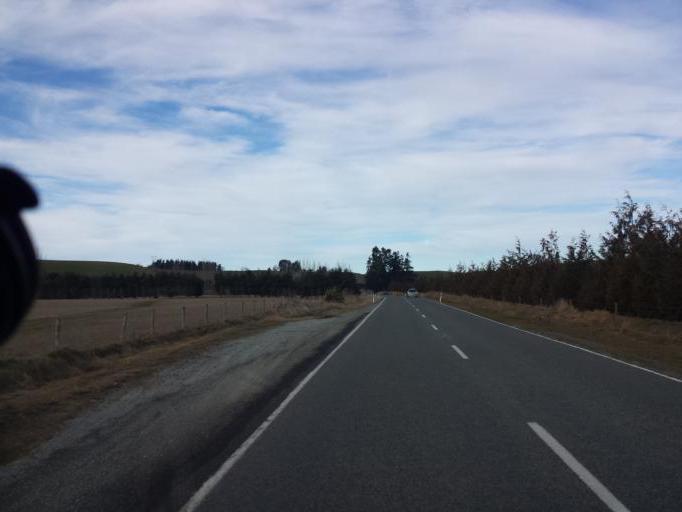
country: NZ
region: Canterbury
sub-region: Timaru District
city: Pleasant Point
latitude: -44.0867
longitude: 170.9864
